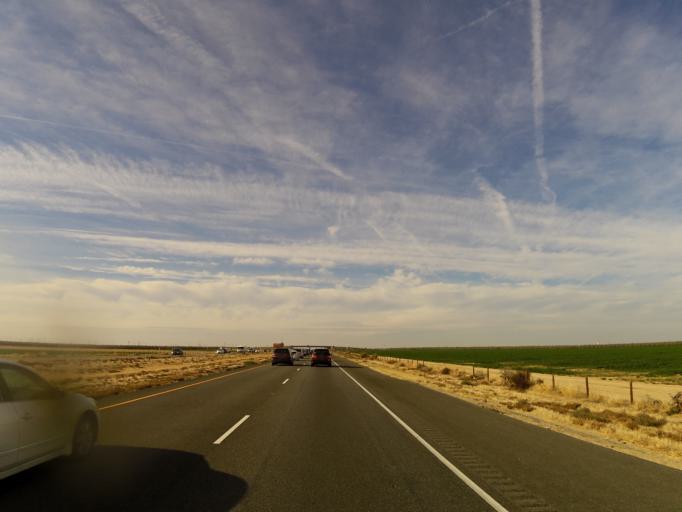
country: US
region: California
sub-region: Kern County
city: Buttonwillow
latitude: 35.4501
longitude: -119.4673
